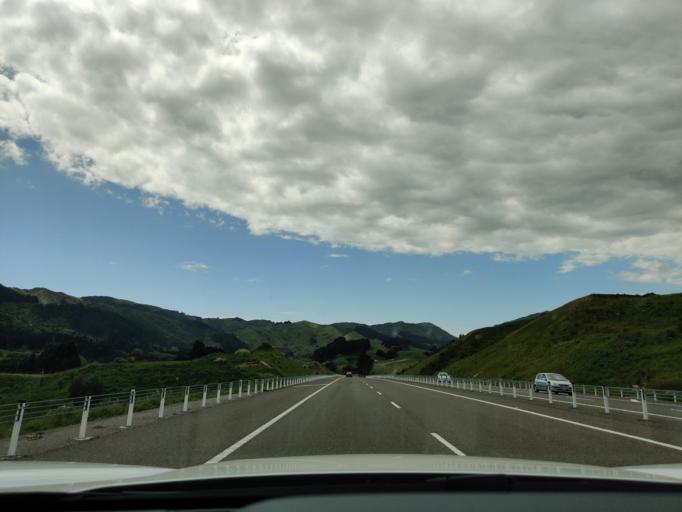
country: NZ
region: Wellington
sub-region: Porirua City
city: Porirua
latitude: -41.0739
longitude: 174.9420
